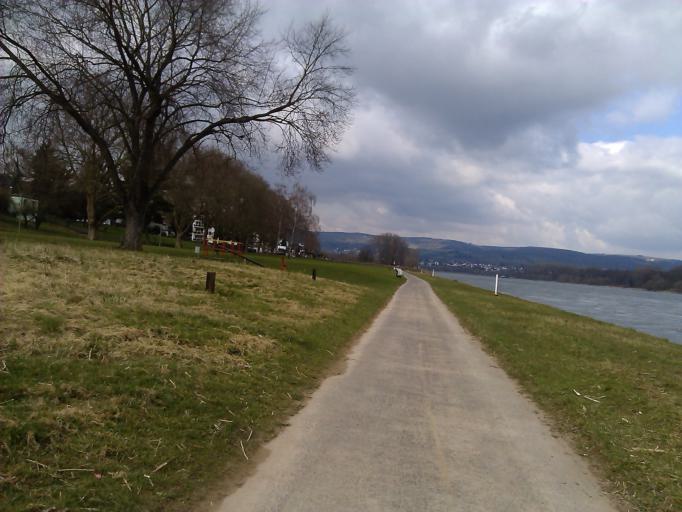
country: DE
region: Rheinland-Pfalz
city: Weissenthurm
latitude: 50.4225
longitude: 7.4532
